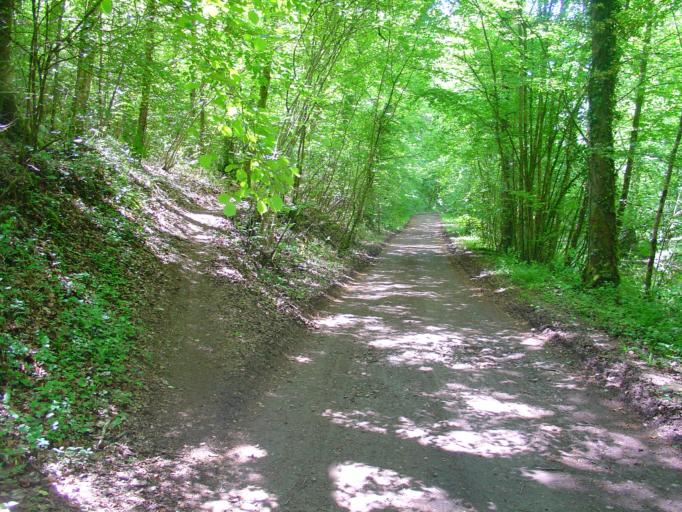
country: FR
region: Lorraine
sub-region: Departement de Meurthe-et-Moselle
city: Villey-Saint-Etienne
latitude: 48.8374
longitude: 5.9113
